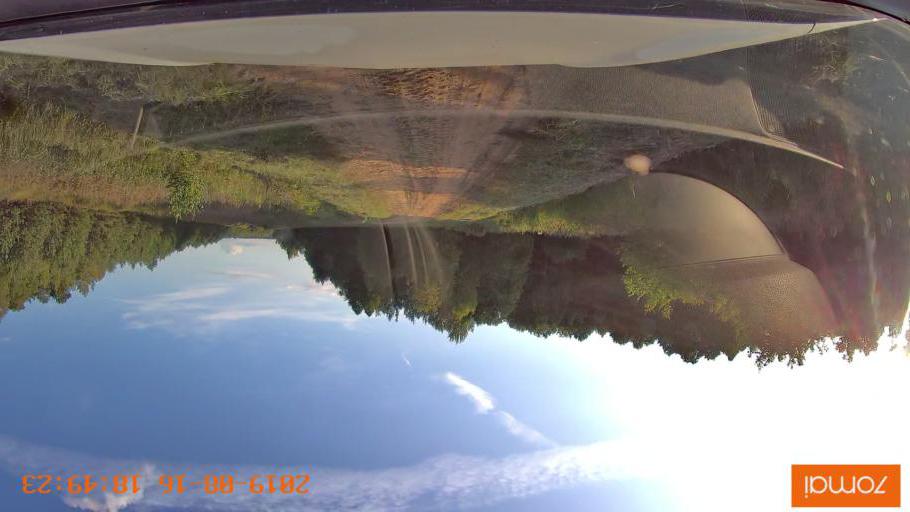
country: BY
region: Mogilev
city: Asipovichy
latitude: 53.2365
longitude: 28.6657
